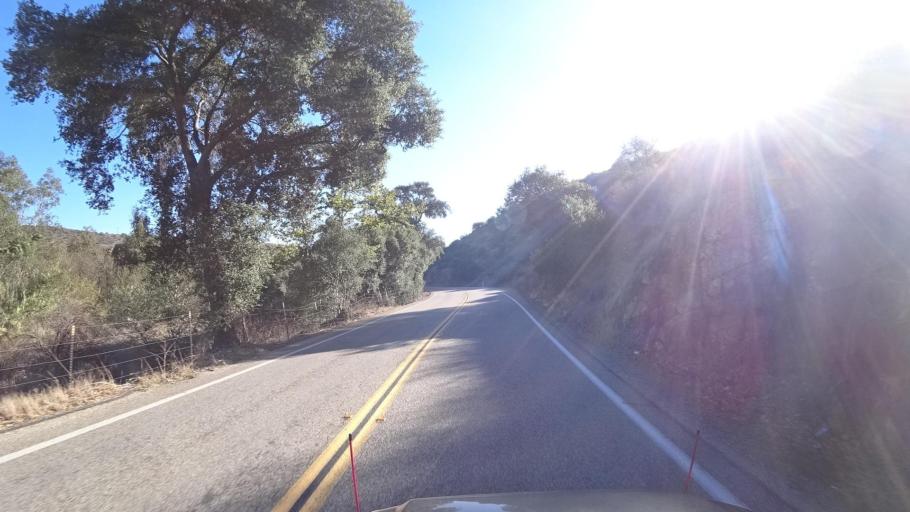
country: US
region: California
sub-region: San Diego County
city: Jamul
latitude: 32.6524
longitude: -116.8598
